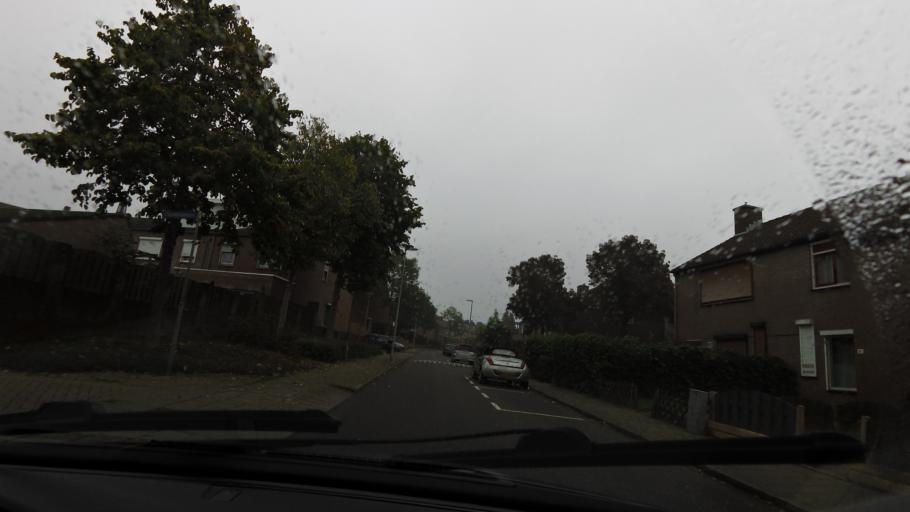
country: NL
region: Limburg
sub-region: Gemeente Heerlen
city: Heerlen
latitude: 50.8975
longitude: 5.9623
